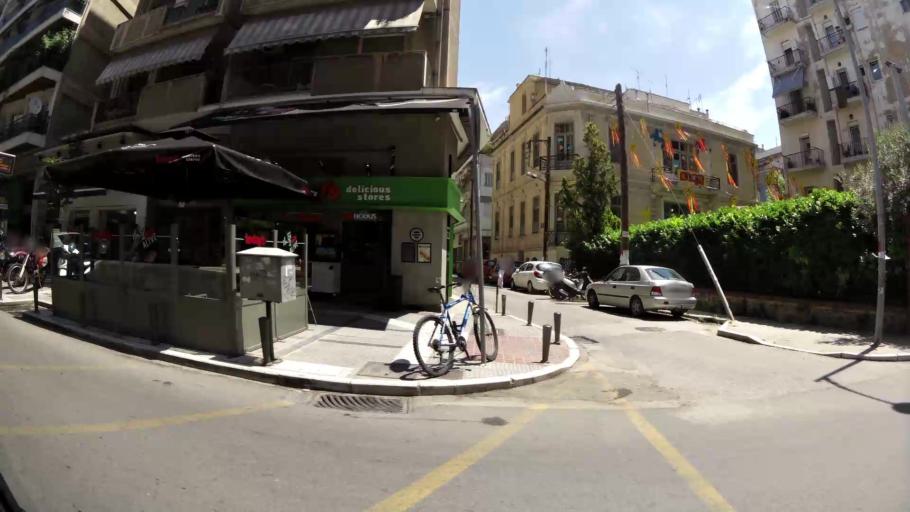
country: GR
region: Central Macedonia
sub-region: Nomos Thessalonikis
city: Triandria
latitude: 40.6107
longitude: 22.9537
